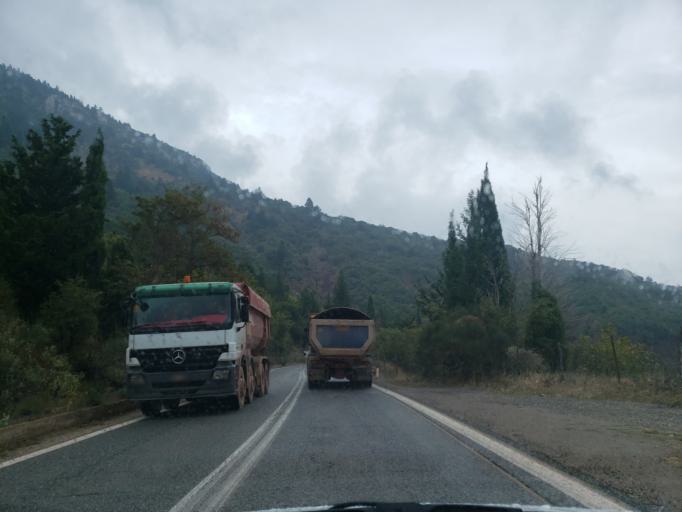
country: GR
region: Central Greece
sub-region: Nomos Fokidos
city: Amfissa
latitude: 38.5833
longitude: 22.3917
